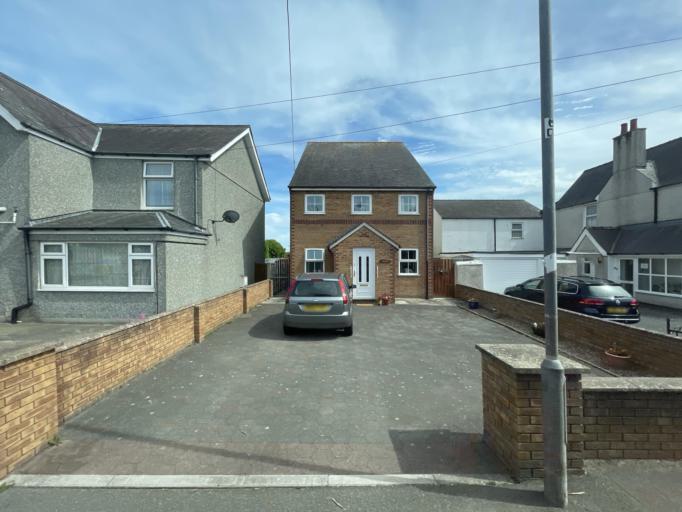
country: GB
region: Wales
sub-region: Anglesey
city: Valley
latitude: 53.2819
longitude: -4.5617
